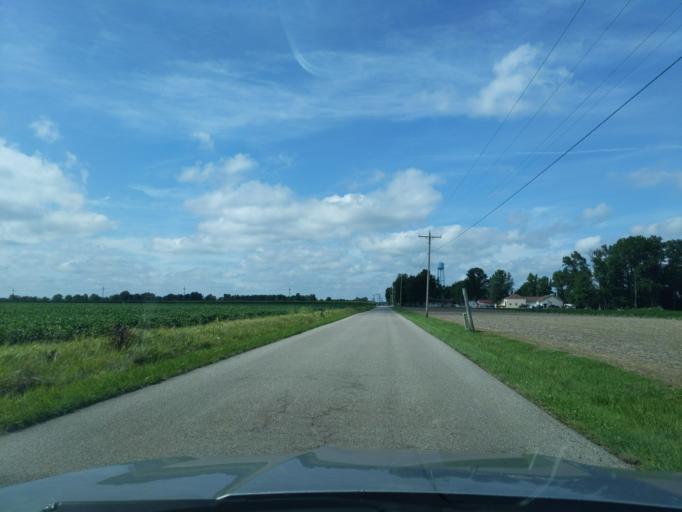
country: US
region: Indiana
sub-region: Ripley County
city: Batesville
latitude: 39.3053
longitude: -85.3477
